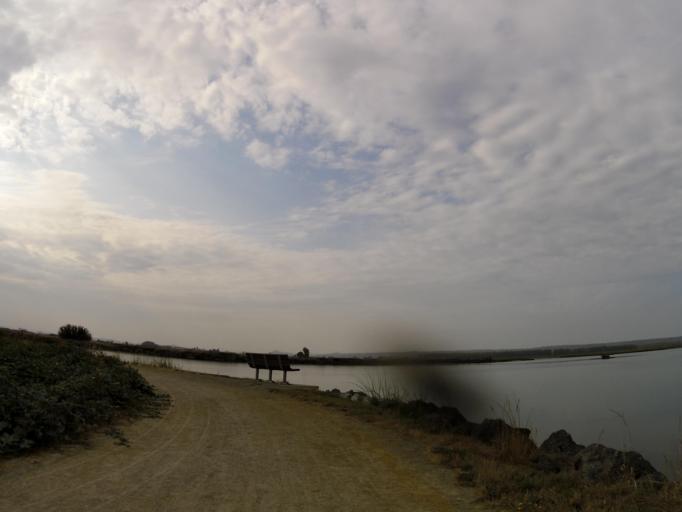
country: US
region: Washington
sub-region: Skagit County
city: Mount Vernon
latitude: 48.4706
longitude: -122.4699
